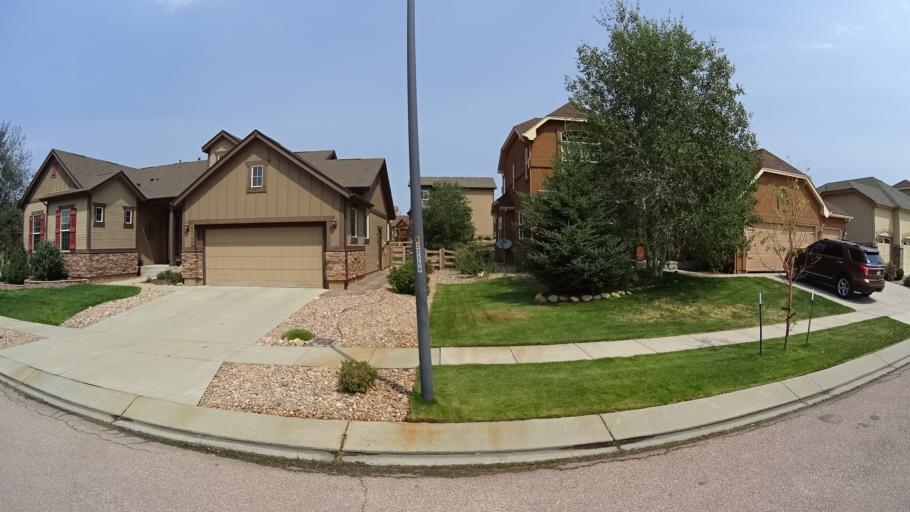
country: US
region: Colorado
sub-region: El Paso County
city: Black Forest
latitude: 38.9673
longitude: -104.7151
